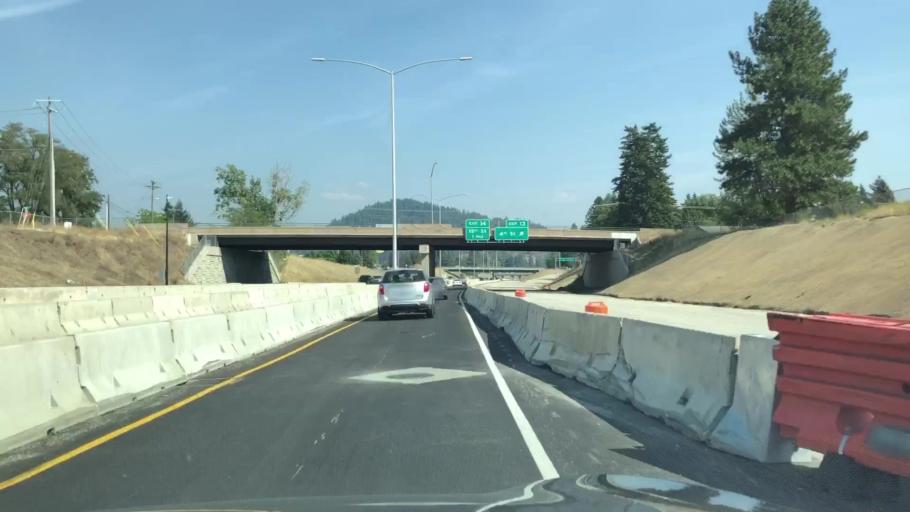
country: US
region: Idaho
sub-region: Kootenai County
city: Coeur d'Alene
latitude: 47.6984
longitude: -116.7878
